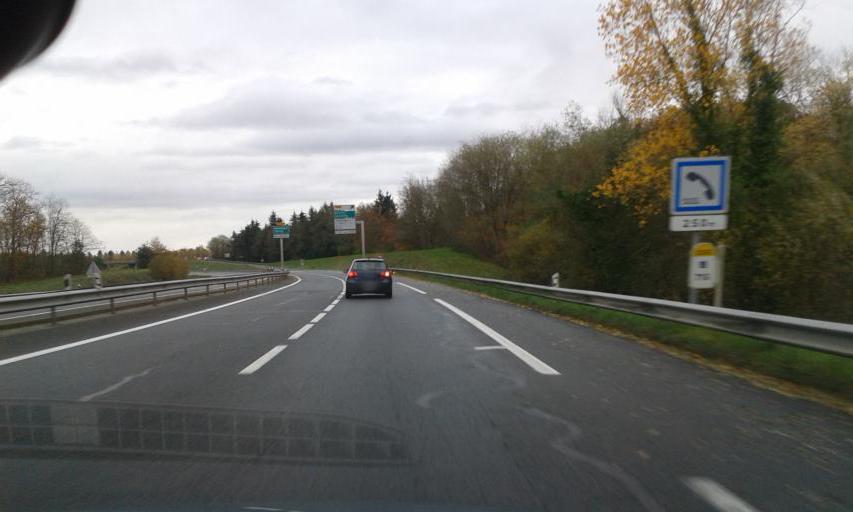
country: FR
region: Centre
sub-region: Departement du Loiret
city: Chateauneuf-sur-Loire
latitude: 47.8824
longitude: 2.2289
